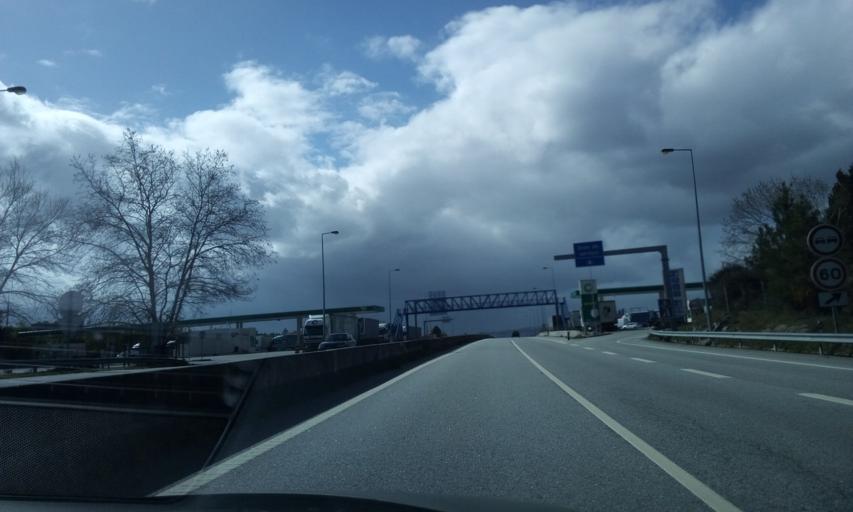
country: PT
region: Viseu
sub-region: Mangualde
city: Mangualde
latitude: 40.6251
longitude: -7.7793
